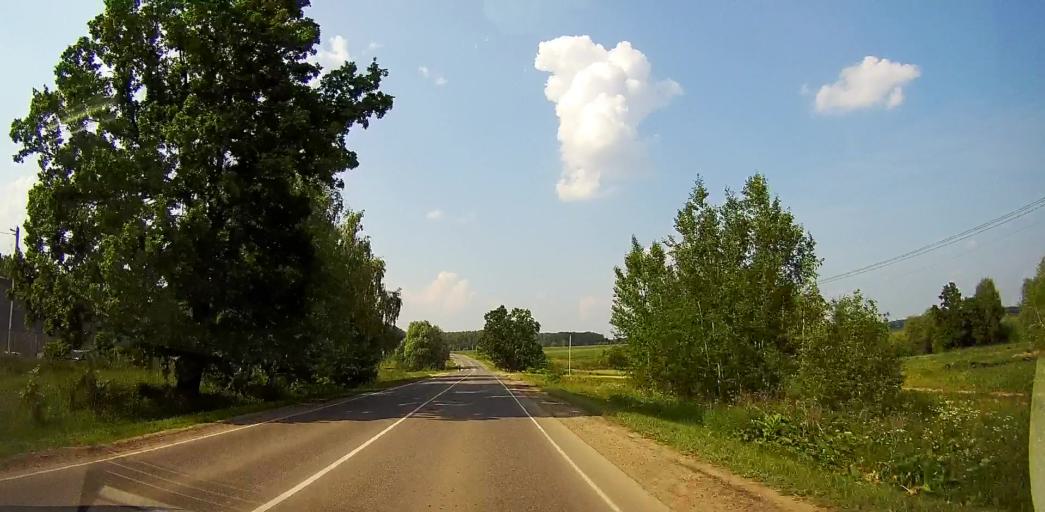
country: RU
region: Moskovskaya
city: Il'inskoye
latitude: 55.2039
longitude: 37.9627
